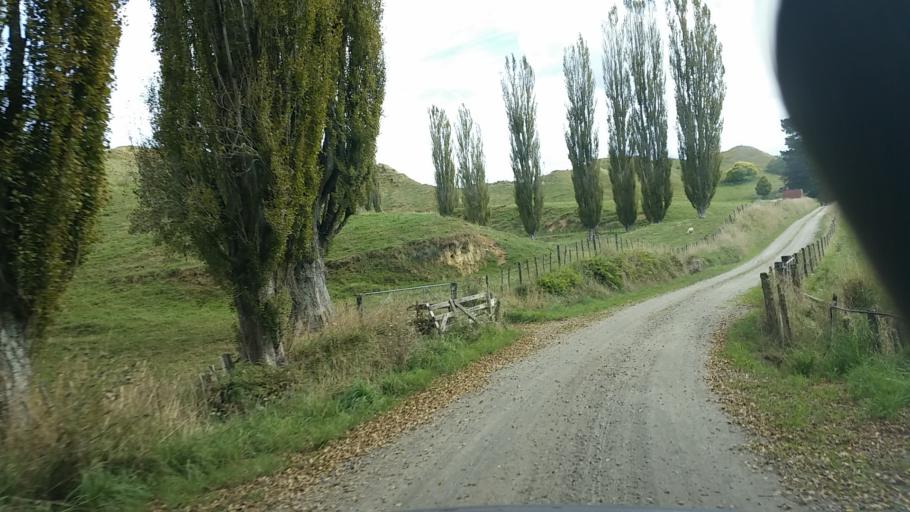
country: NZ
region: Taranaki
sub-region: South Taranaki District
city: Eltham
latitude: -39.2586
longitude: 174.5592
